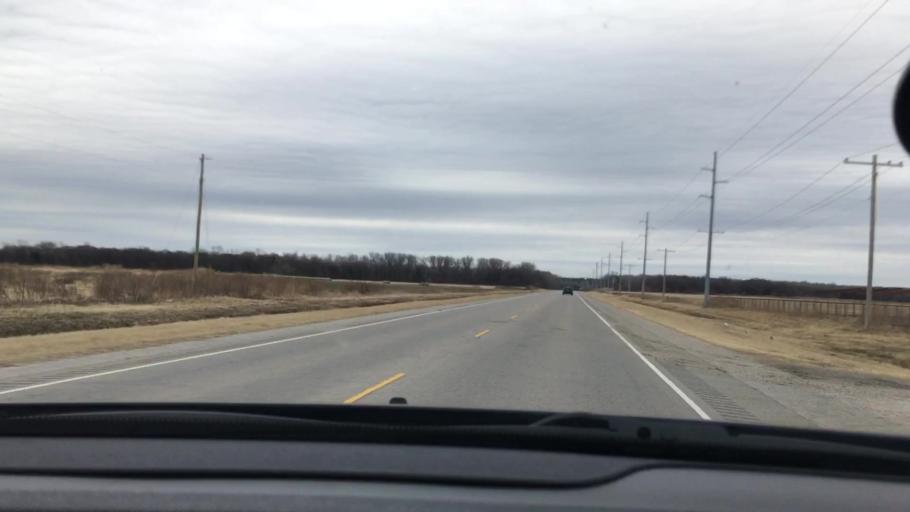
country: US
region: Oklahoma
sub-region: Marshall County
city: Oakland
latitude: 34.2088
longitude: -96.8022
